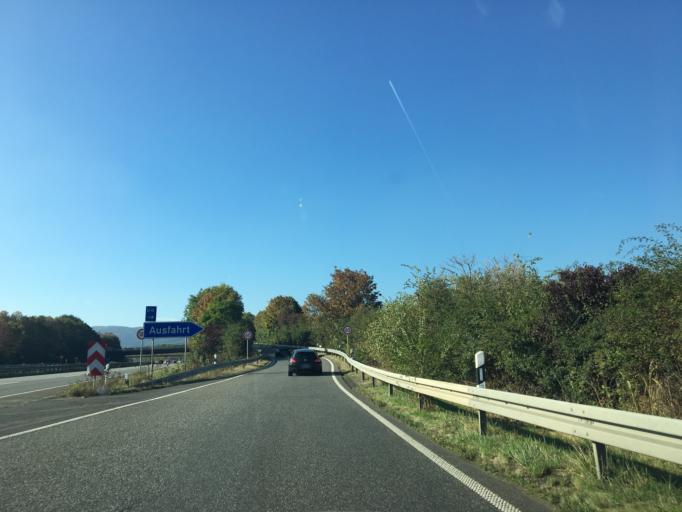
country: DE
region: Hesse
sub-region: Regierungsbezirk Darmstadt
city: Oberursel
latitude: 50.2148
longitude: 8.5804
